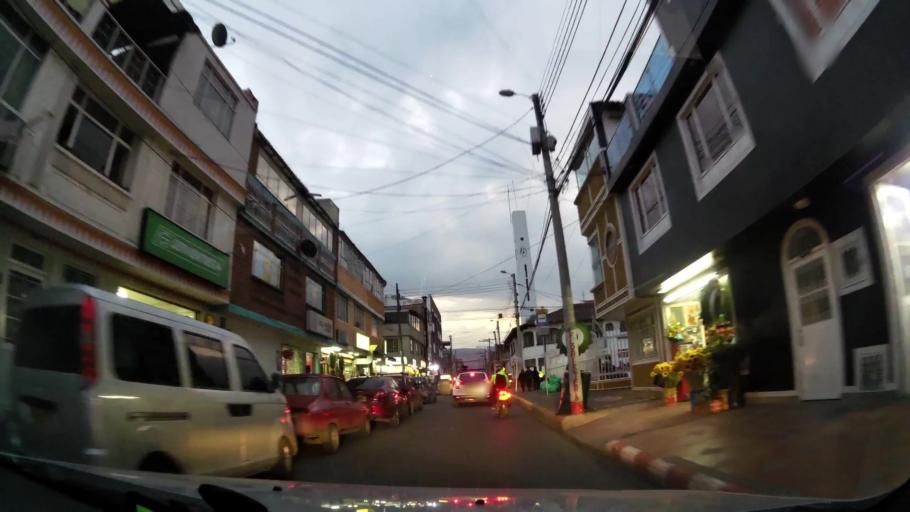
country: CO
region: Bogota D.C.
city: Bogota
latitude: 4.5813
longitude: -74.1351
